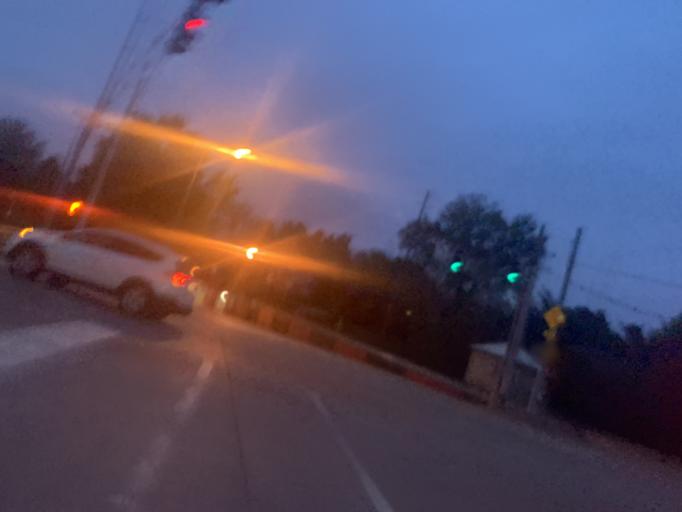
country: US
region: Kentucky
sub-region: Jefferson County
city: Audubon Park
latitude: 38.2139
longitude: -85.7642
